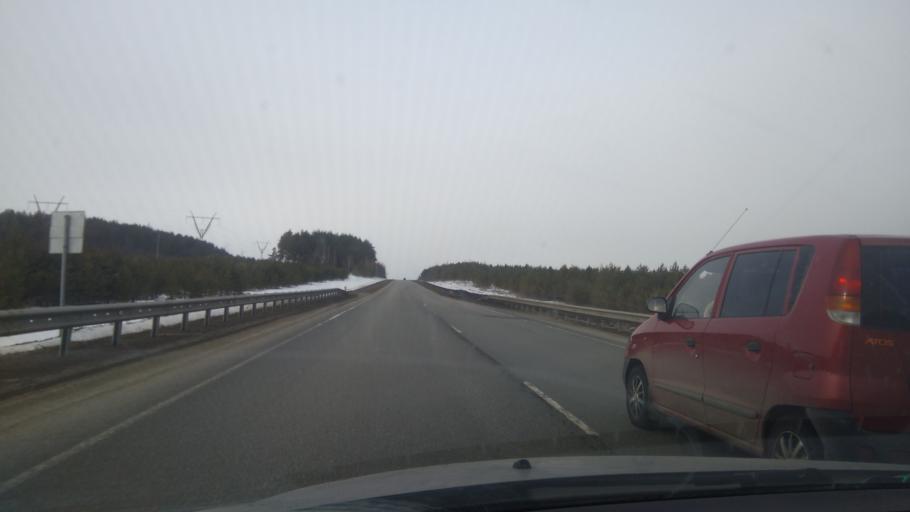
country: RU
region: Sverdlovsk
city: Achit
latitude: 56.7801
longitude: 57.9384
